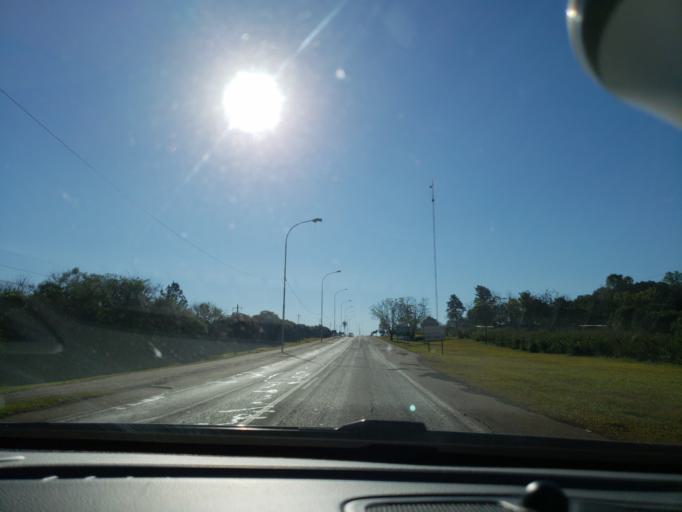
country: AR
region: Misiones
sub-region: Departamento de Apostoles
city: San Jose
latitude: -27.7504
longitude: -55.7787
